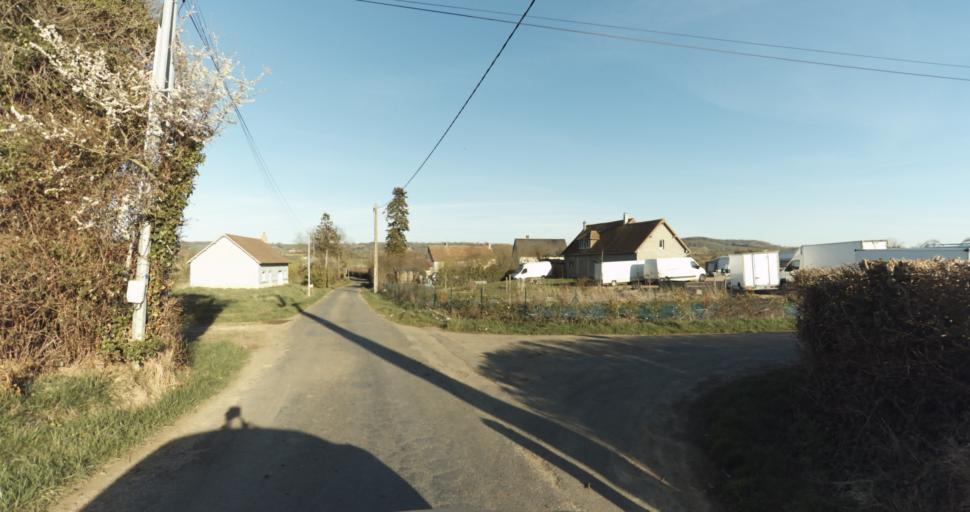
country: FR
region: Lower Normandy
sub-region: Departement de l'Orne
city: Trun
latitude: 48.9150
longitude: 0.0164
